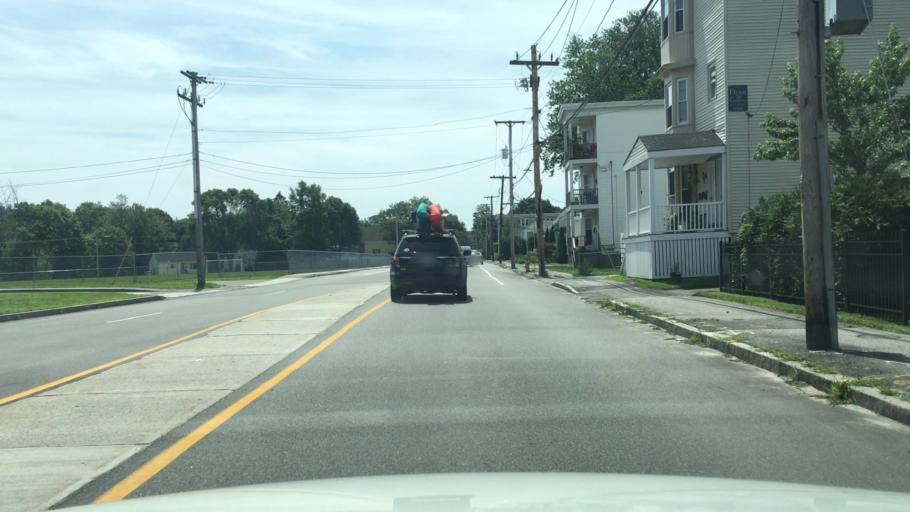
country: US
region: Maine
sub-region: Cumberland County
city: South Portland
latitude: 43.6338
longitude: -70.2521
